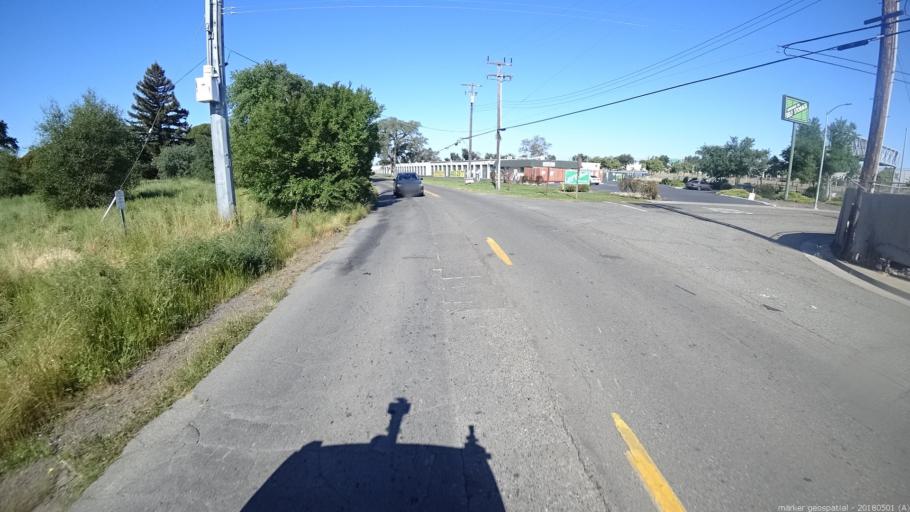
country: US
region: California
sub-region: Sacramento County
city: Arden-Arcade
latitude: 38.6435
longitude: -121.3878
